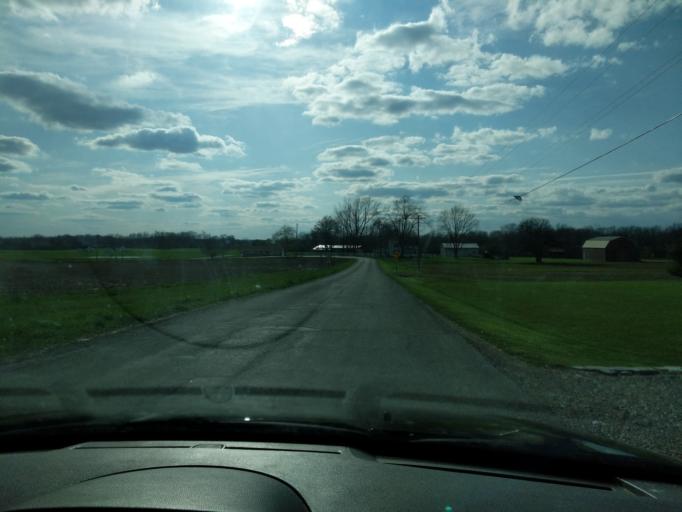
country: US
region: Ohio
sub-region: Champaign County
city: Urbana
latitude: 40.1322
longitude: -83.7265
